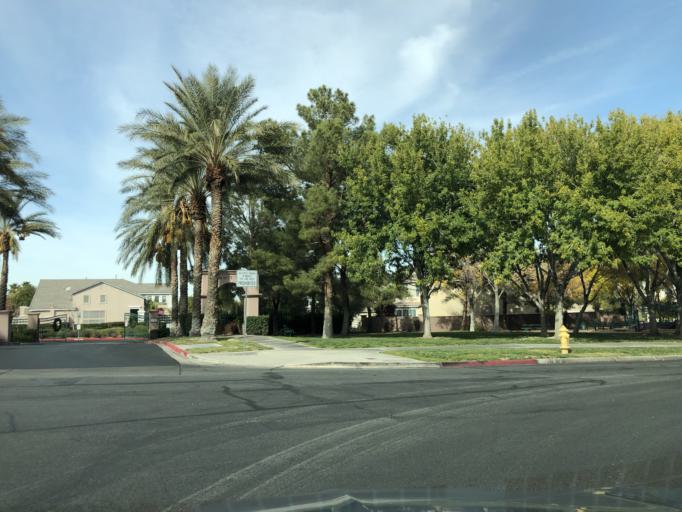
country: US
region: Nevada
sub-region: Clark County
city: Whitney
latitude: 36.0140
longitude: -115.0868
